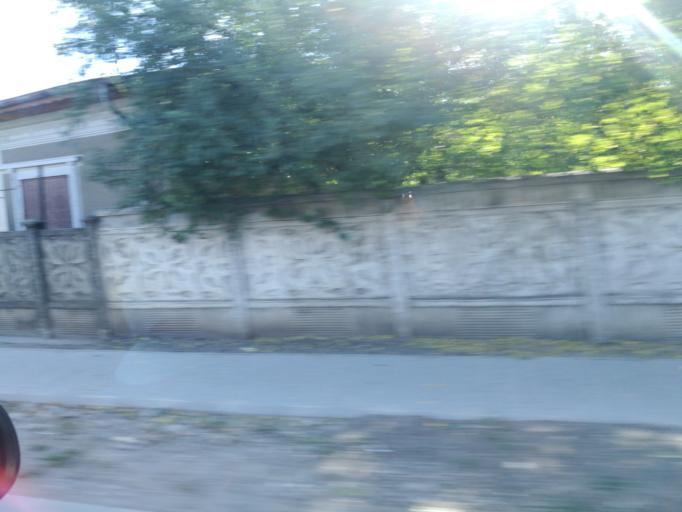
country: RO
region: Ilfov
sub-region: Comuna Dragomiresti-Vale
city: Dragomiresti-Deal
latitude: 44.4629
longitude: 25.9400
